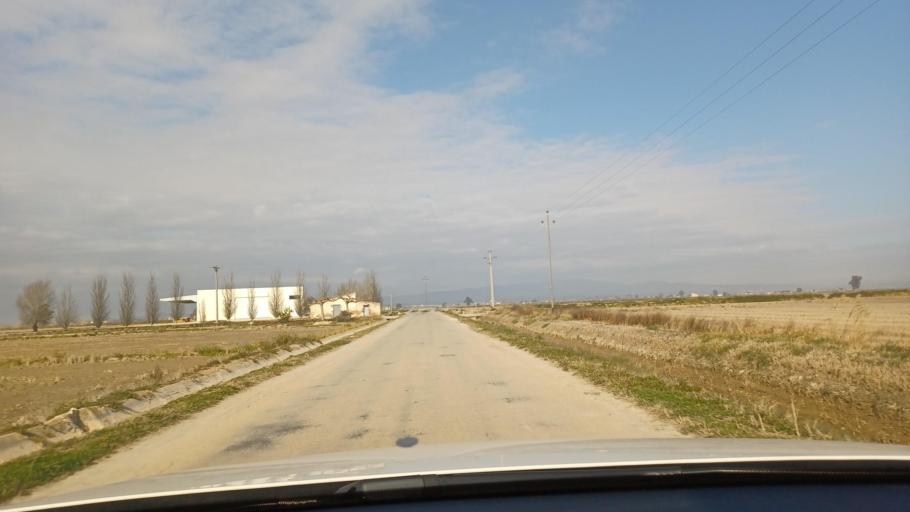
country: ES
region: Catalonia
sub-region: Provincia de Tarragona
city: Deltebre
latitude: 40.6805
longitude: 0.6582
